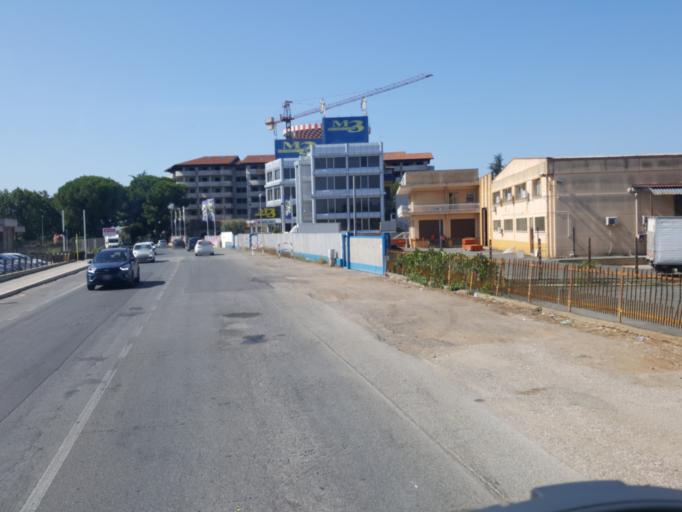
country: IT
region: Latium
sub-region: Citta metropolitana di Roma Capitale
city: Area Produttiva
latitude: 41.6868
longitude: 12.5132
